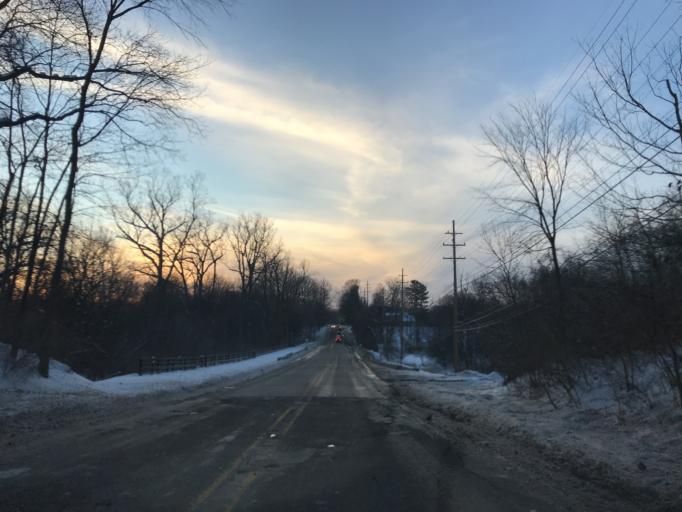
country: US
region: Michigan
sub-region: Oakland County
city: Franklin
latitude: 42.4569
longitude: -83.3043
